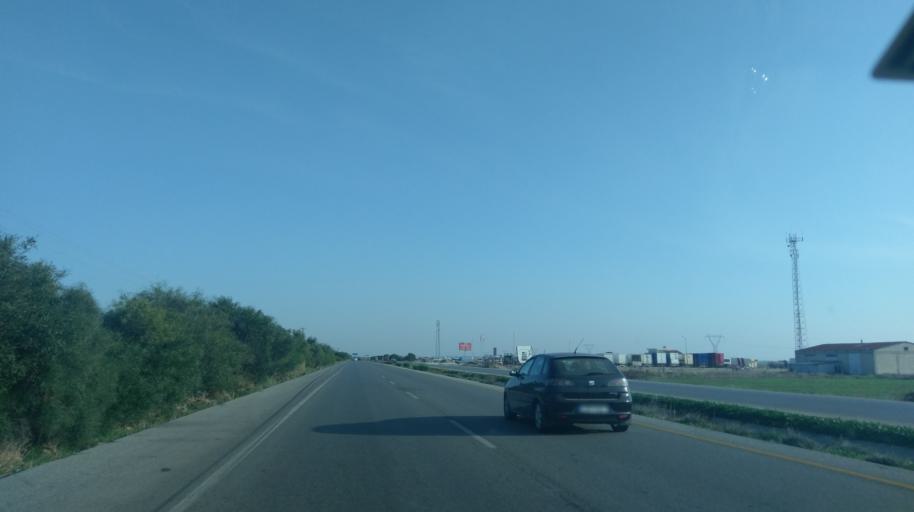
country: CY
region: Ammochostos
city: Acheritou
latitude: 35.1605
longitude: 33.8343
